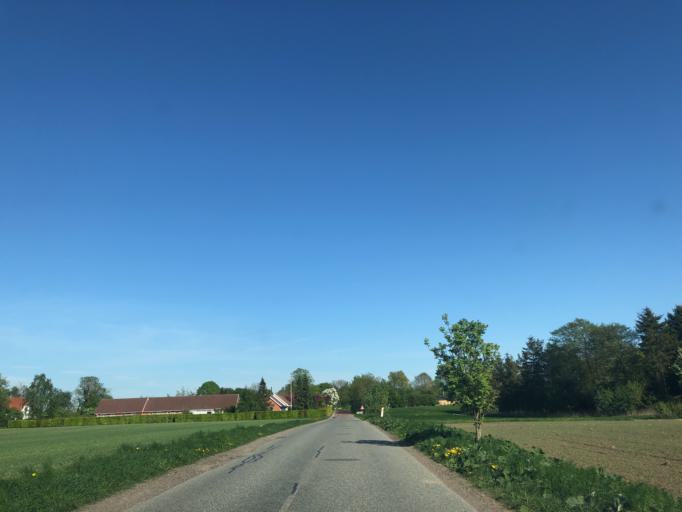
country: DK
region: Zealand
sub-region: Ringsted Kommune
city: Ringsted
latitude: 55.4493
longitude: 11.7240
